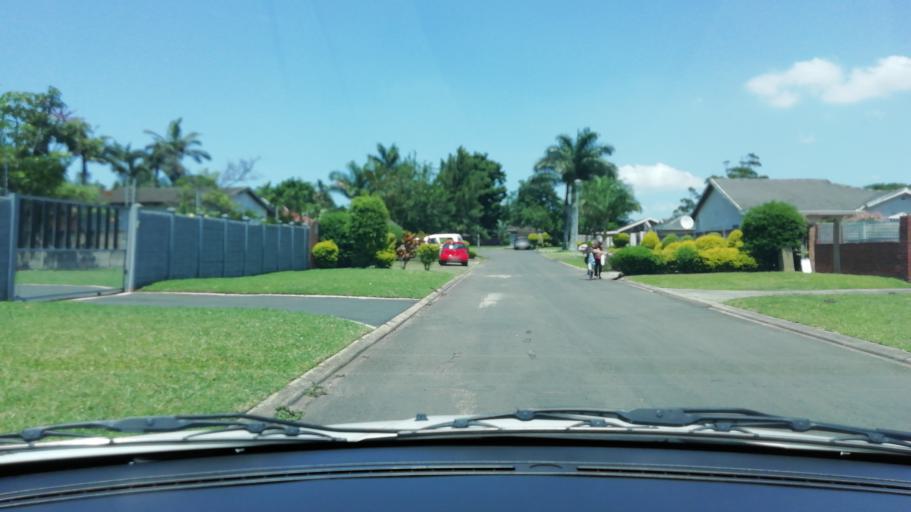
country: ZA
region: KwaZulu-Natal
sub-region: uThungulu District Municipality
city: Richards Bay
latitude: -28.7355
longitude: 32.0548
